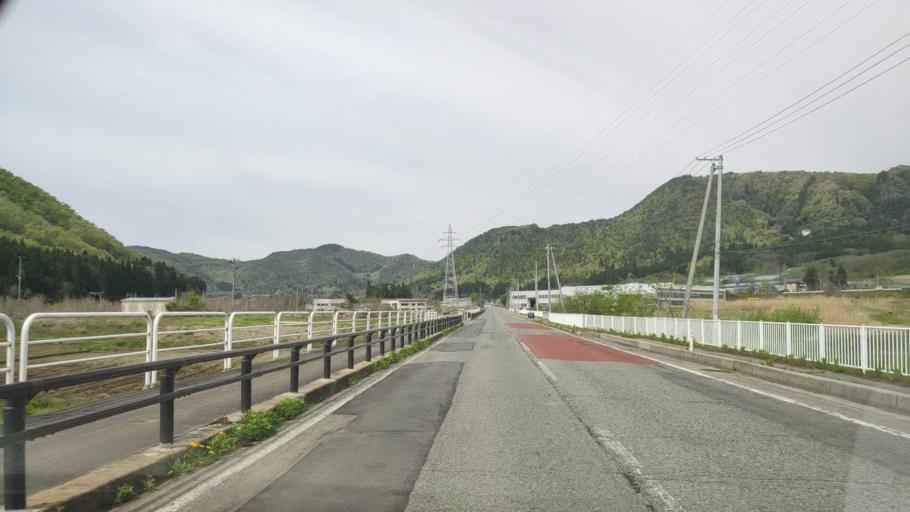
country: JP
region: Yamagata
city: Takahata
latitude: 38.0924
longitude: 140.1989
